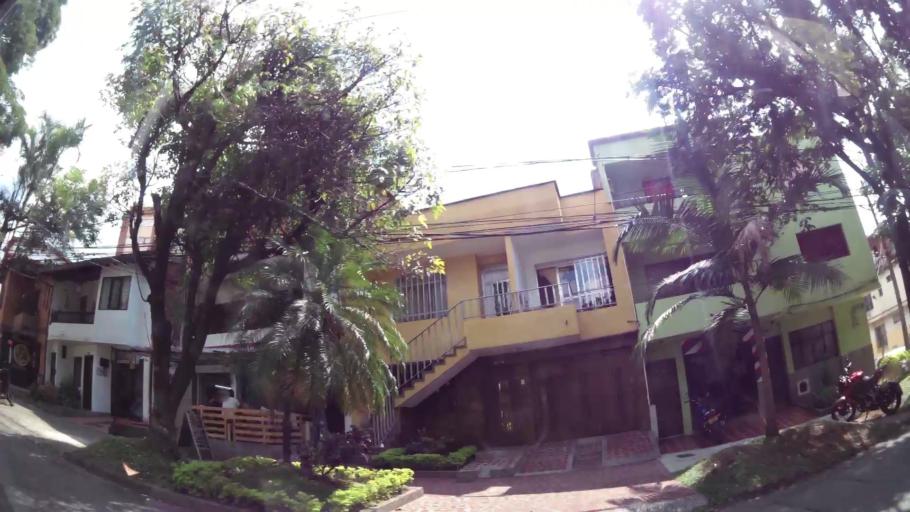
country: CO
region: Antioquia
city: Envigado
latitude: 6.1695
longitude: -75.5909
